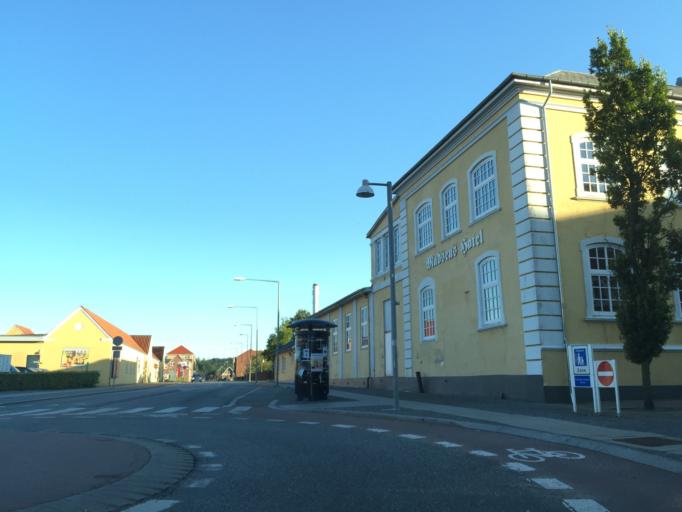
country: DK
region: Central Jutland
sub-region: Viborg Kommune
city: Bjerringbro
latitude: 56.3742
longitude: 9.6554
